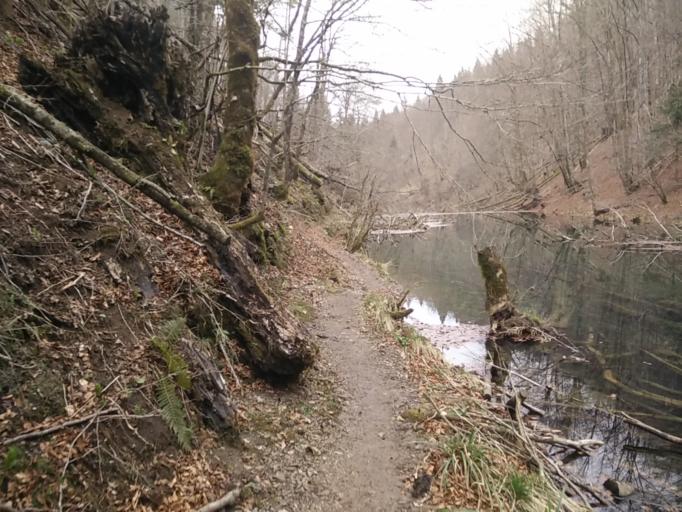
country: HR
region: Primorsko-Goranska
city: Vrbovsko
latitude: 45.3483
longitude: 15.0606
